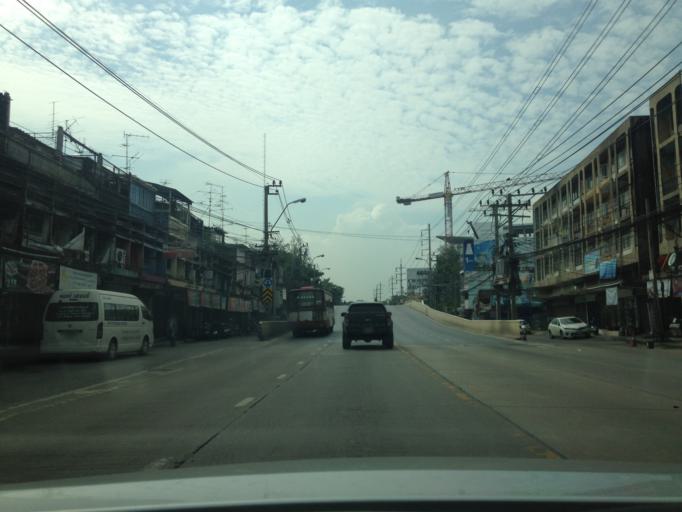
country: TH
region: Bangkok
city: Bang Sue
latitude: 13.8011
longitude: 100.5213
